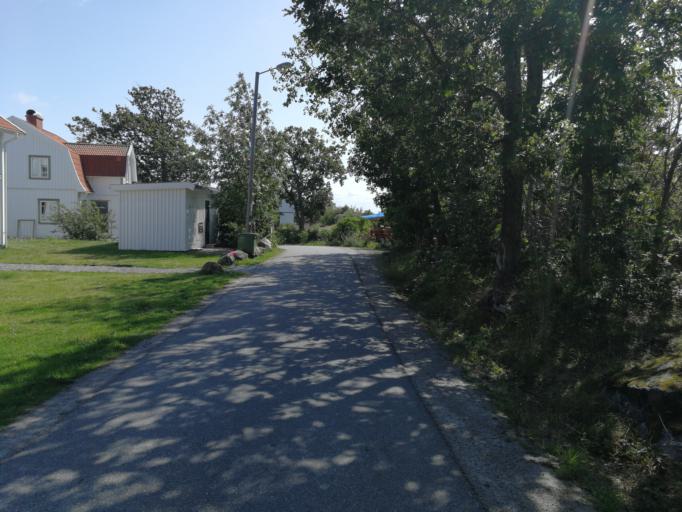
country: NO
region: Ostfold
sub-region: Hvaler
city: Skjaerhalden
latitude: 58.8943
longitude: 11.0455
